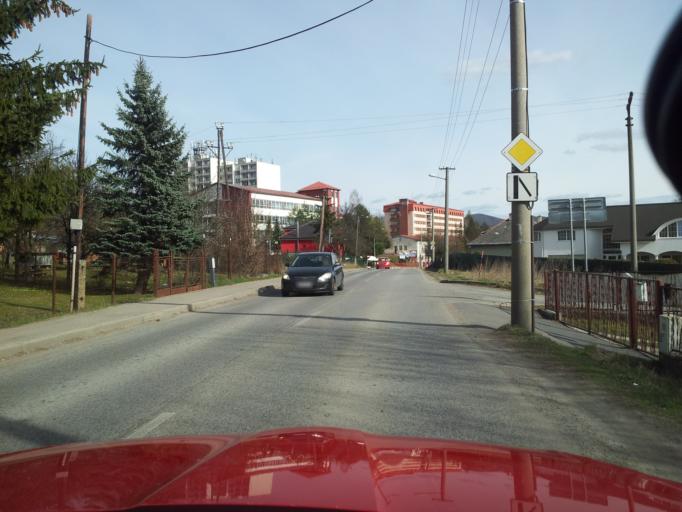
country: SK
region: Banskobystricky
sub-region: Okres Banska Bystrica
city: Banska Bystrica
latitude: 48.7410
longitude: 19.1237
